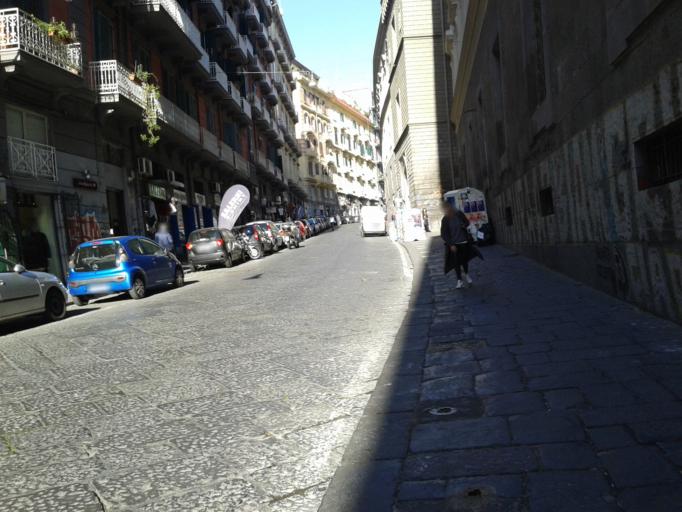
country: IT
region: Campania
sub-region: Provincia di Napoli
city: Napoli
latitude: 40.8457
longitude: 14.2562
